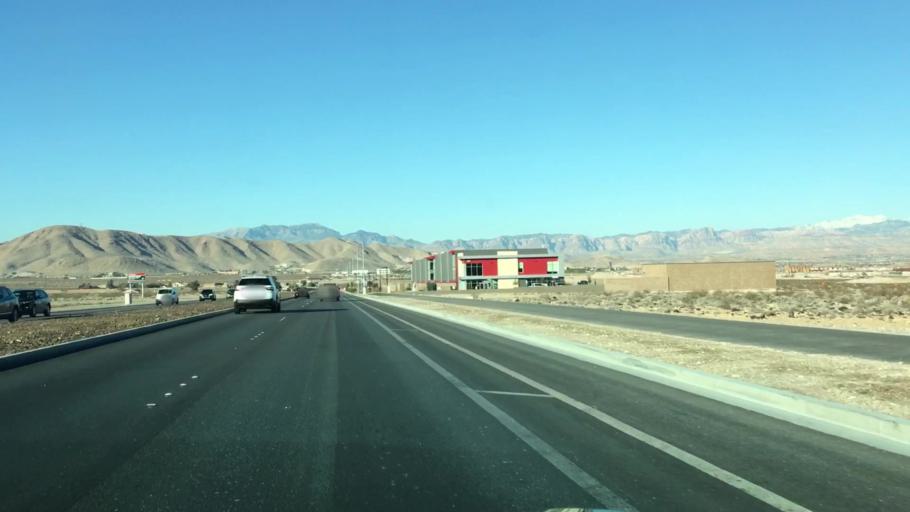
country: US
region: Nevada
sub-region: Clark County
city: Enterprise
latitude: 35.9600
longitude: -115.1418
